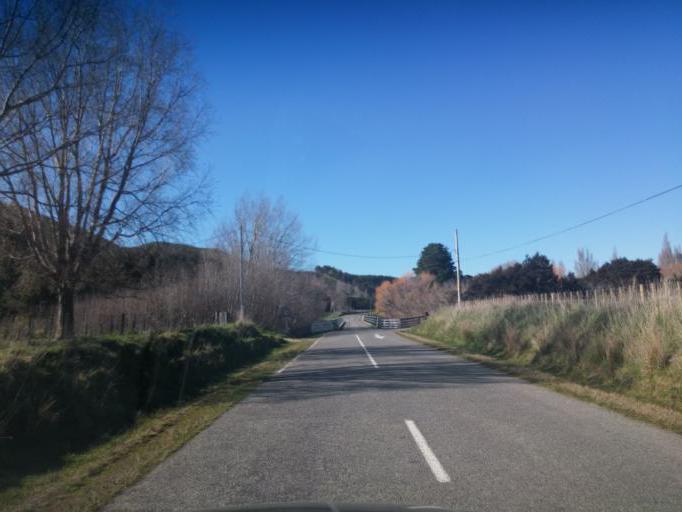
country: NZ
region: Wellington
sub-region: South Wairarapa District
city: Waipawa
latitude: -41.4301
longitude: 175.5086
